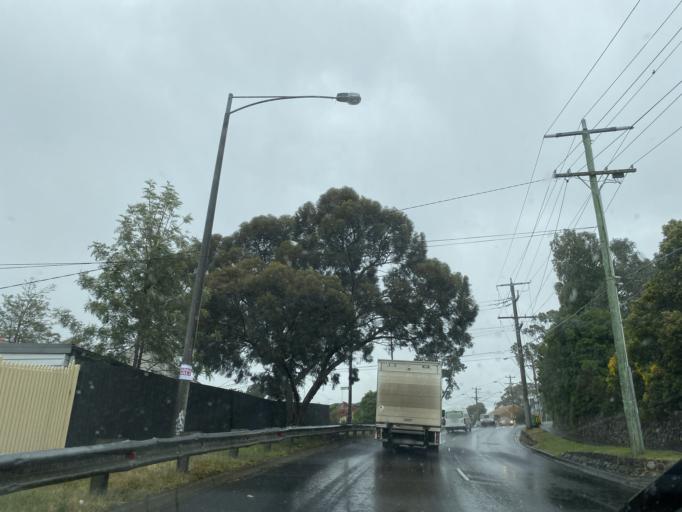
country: AU
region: Victoria
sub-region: Banyule
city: Montmorency
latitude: -37.7247
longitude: 145.1123
